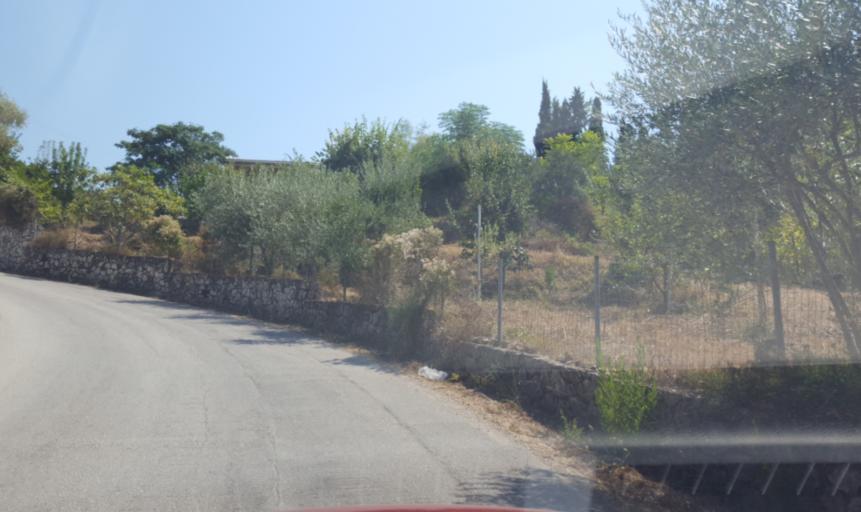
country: GR
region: Ionian Islands
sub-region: Lefkada
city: Nidri
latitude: 38.6753
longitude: 20.7089
